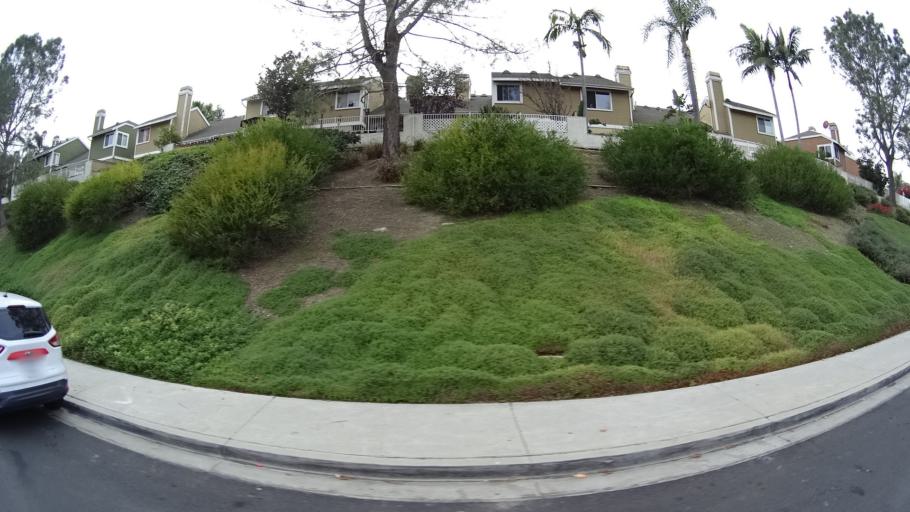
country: US
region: California
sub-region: Orange County
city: Laguna Hills
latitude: 33.5916
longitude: -117.7154
